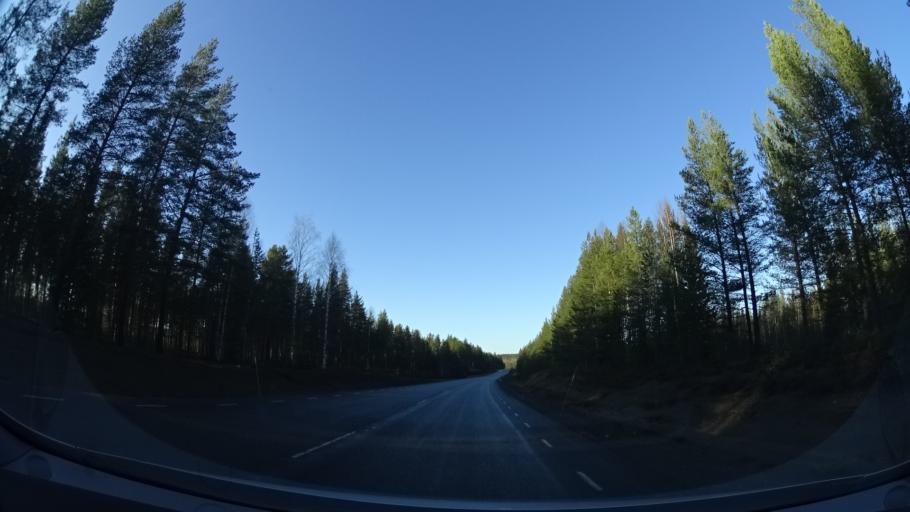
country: SE
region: Vaesterbotten
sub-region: Skelleftea Kommun
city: Langsele
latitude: 64.9083
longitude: 20.1158
